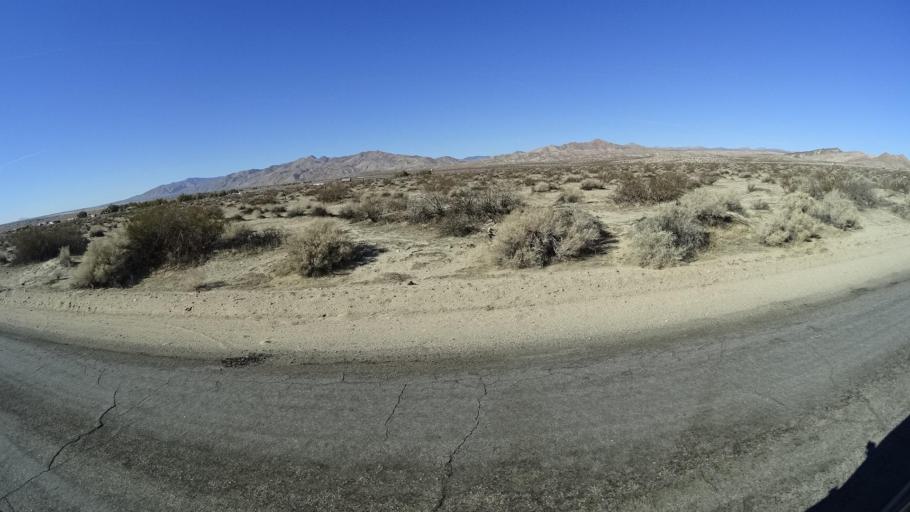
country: US
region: California
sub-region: Kern County
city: California City
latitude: 35.3126
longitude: -117.9503
